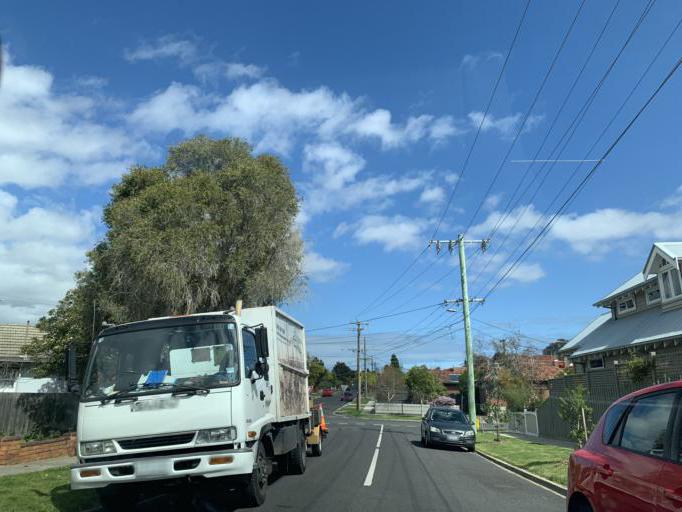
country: AU
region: Victoria
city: Thornbury
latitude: -37.7406
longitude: 144.9872
